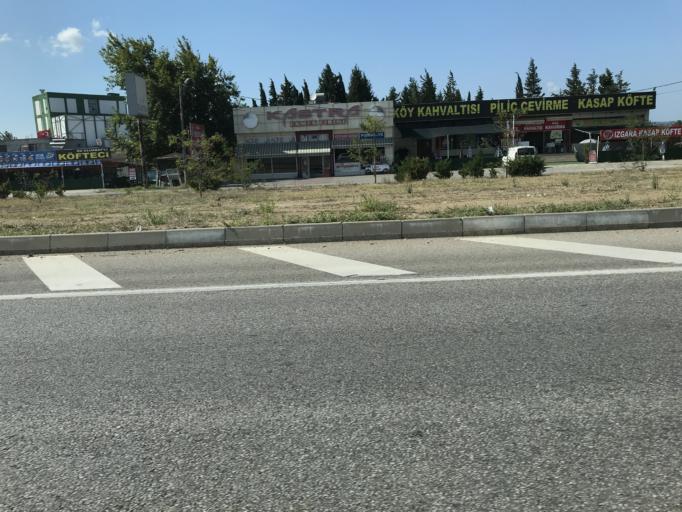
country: TR
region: Bursa
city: Karacabey
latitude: 40.2013
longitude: 28.4264
